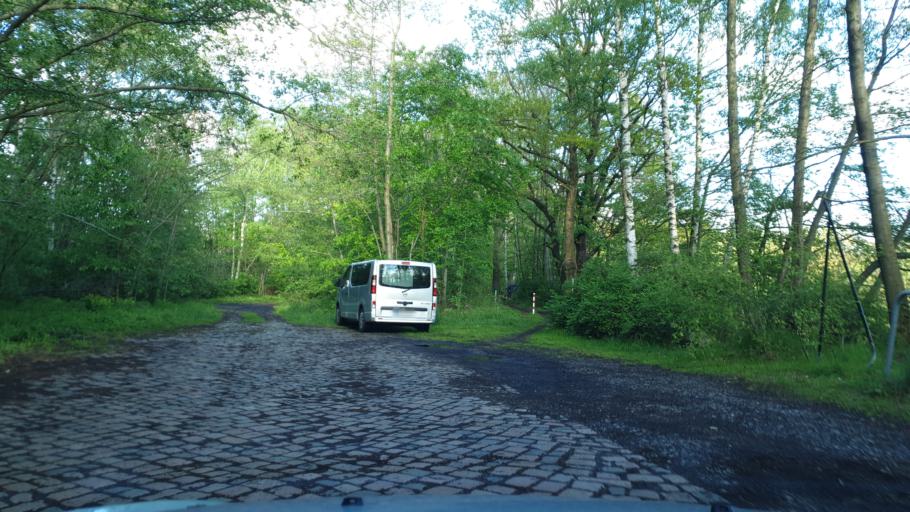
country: DE
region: Saxony
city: Oelsnitz
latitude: 50.7190
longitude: 12.7278
